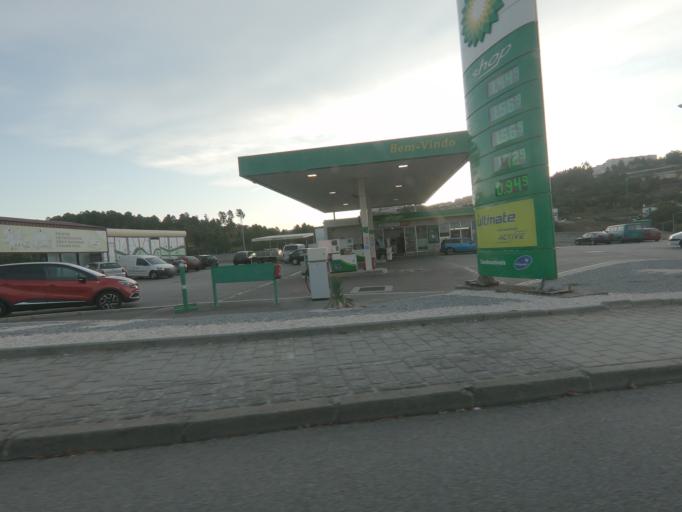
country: PT
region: Vila Real
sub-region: Vila Real
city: Vila Real
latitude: 41.3078
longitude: -7.7567
